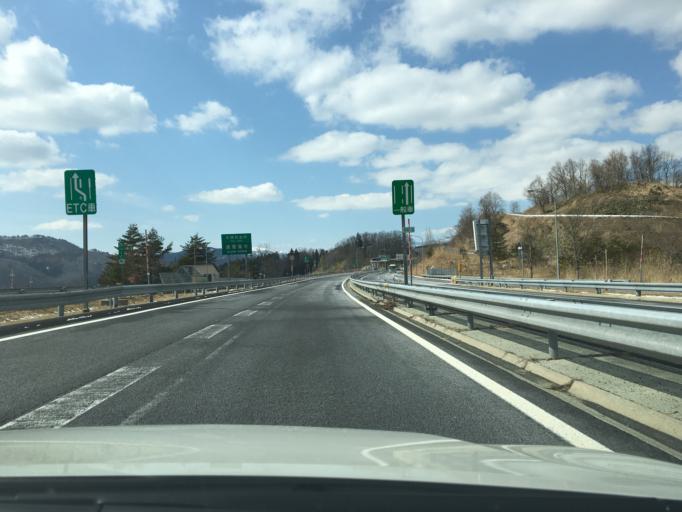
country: JP
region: Yamagata
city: Sagae
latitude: 38.4235
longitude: 140.1665
